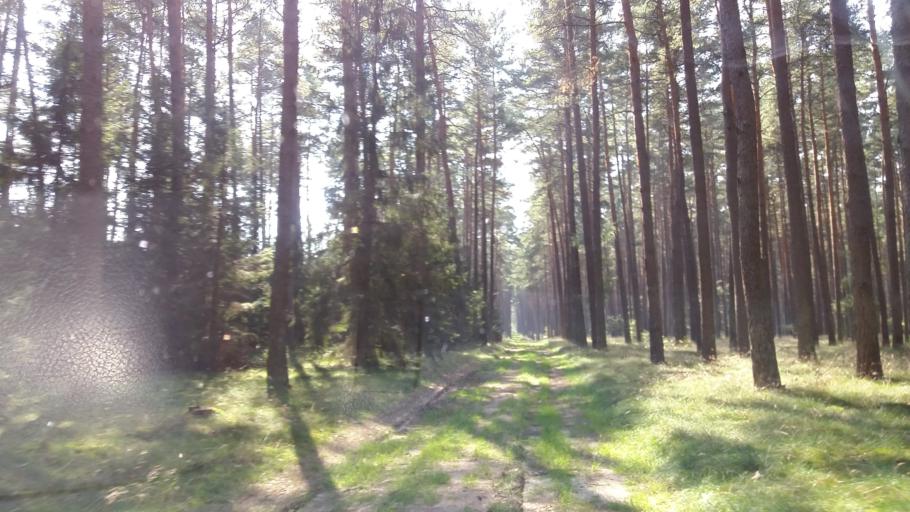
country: PL
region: West Pomeranian Voivodeship
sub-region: Powiat walecki
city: Tuczno
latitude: 53.2223
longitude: 16.0213
